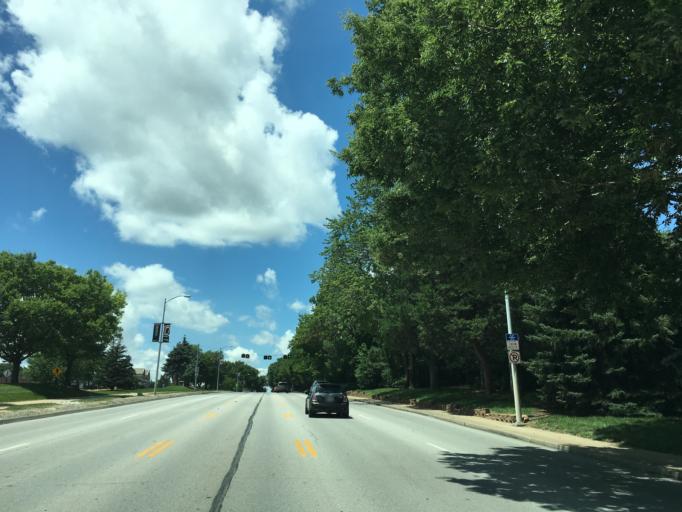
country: US
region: Nebraska
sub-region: Douglas County
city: Ralston
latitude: 41.2596
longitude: -96.0083
